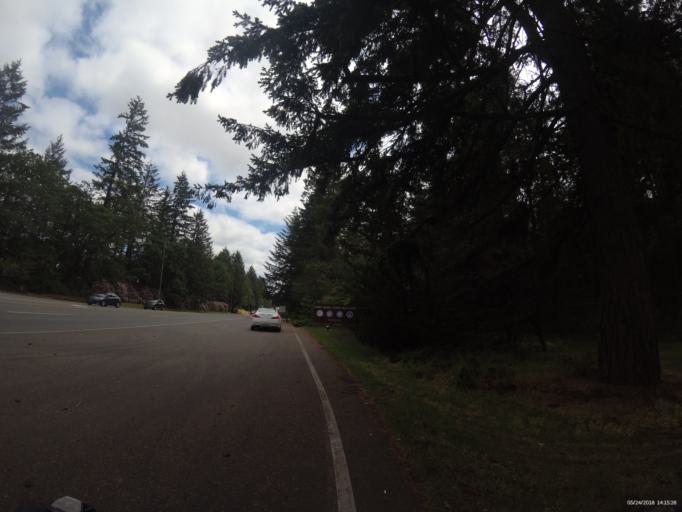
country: US
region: Washington
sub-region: Pierce County
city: McChord Air Force Base
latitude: 47.1392
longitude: -122.5020
